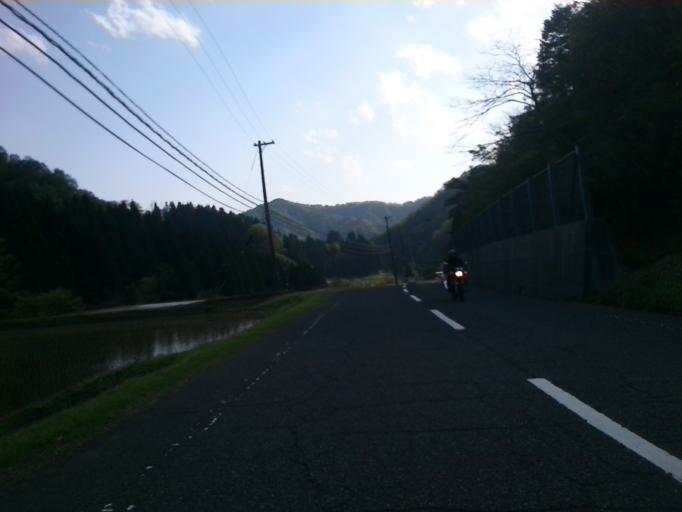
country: JP
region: Kyoto
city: Miyazu
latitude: 35.6912
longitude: 135.1638
